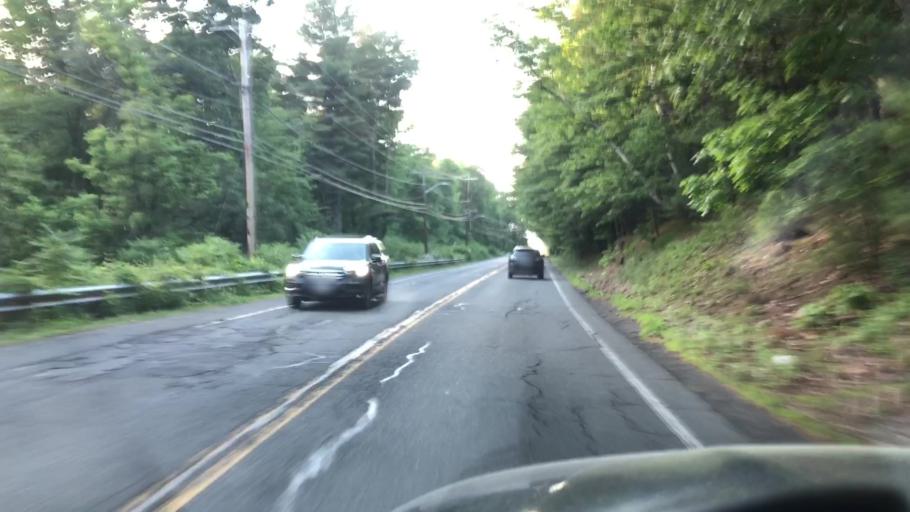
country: US
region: Massachusetts
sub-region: Hampshire County
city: Easthampton
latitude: 42.2325
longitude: -72.6494
